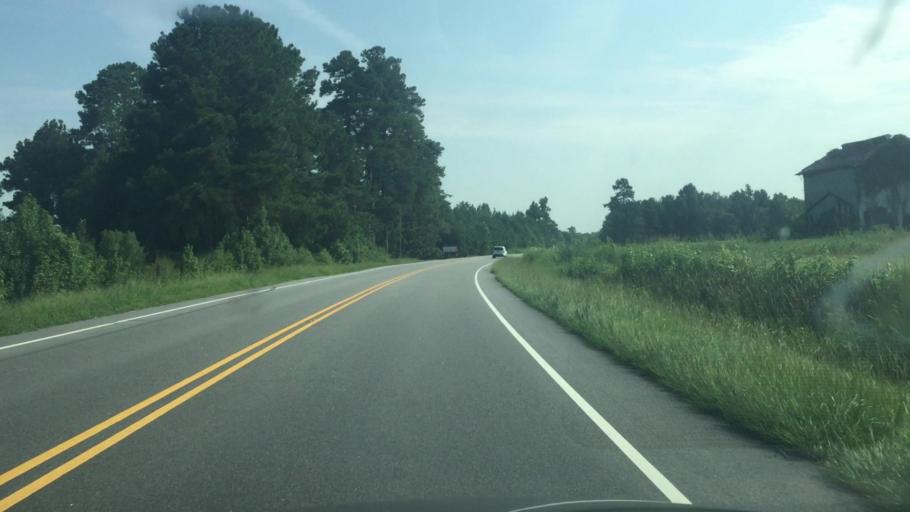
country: US
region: North Carolina
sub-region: Columbus County
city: Tabor City
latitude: 34.1977
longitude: -78.8349
